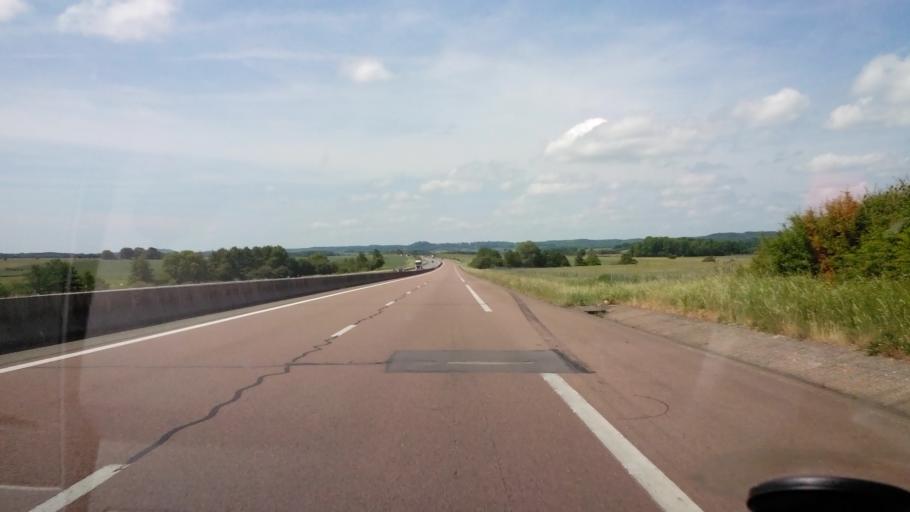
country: FR
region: Champagne-Ardenne
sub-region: Departement de la Haute-Marne
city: Avrecourt
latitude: 48.0407
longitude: 5.5633
